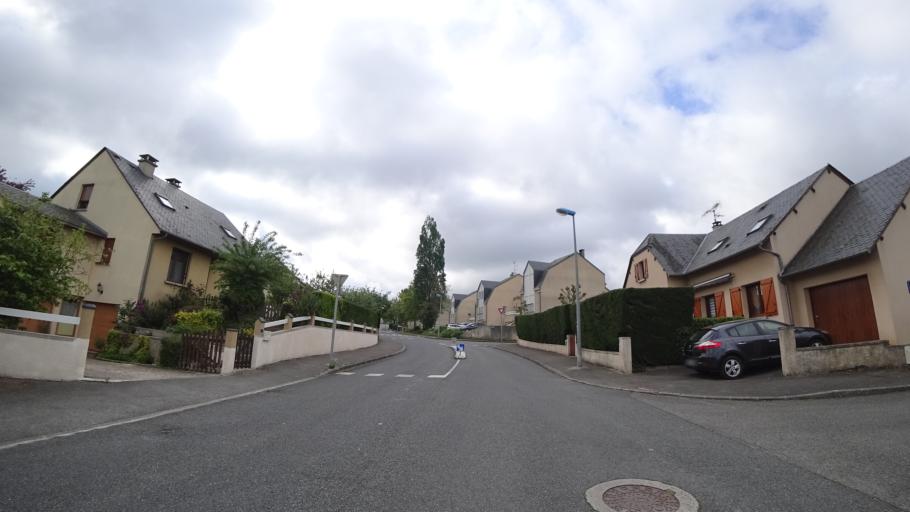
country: FR
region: Midi-Pyrenees
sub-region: Departement de l'Aveyron
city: Rodez
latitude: 44.3663
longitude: 2.5842
